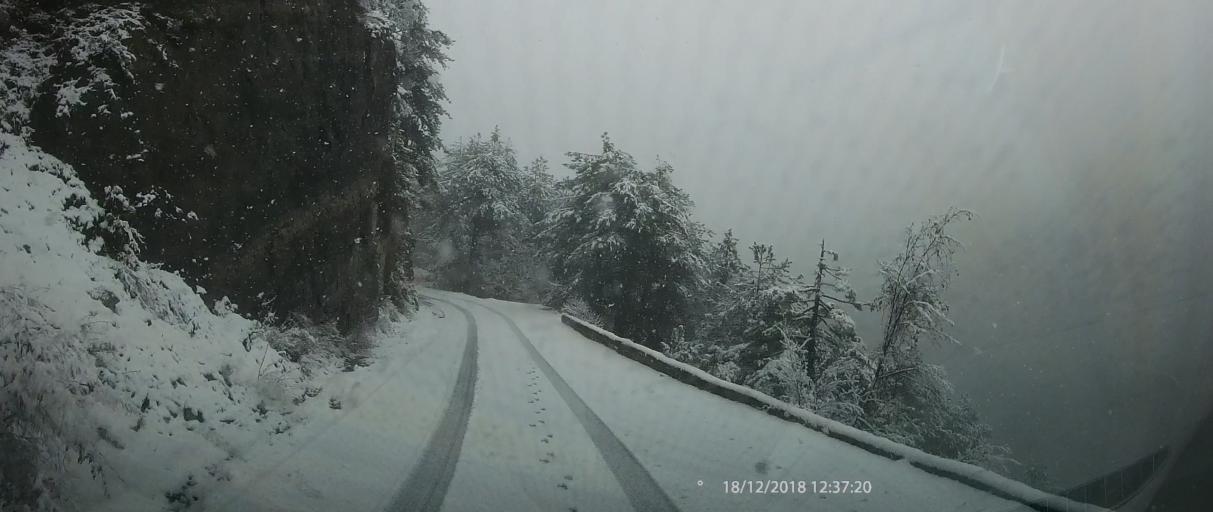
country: GR
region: Central Macedonia
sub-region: Nomos Pierias
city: Litochoro
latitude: 40.0883
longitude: 22.4112
